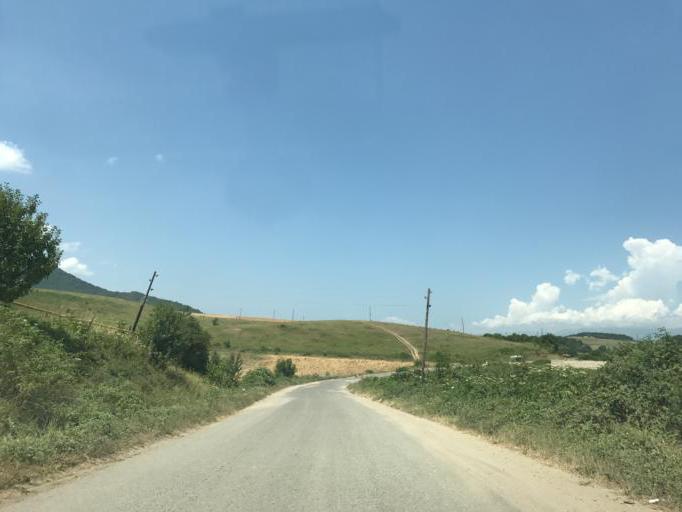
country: AZ
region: Tartar Rayon
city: Martakert
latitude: 40.1064
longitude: 46.6427
